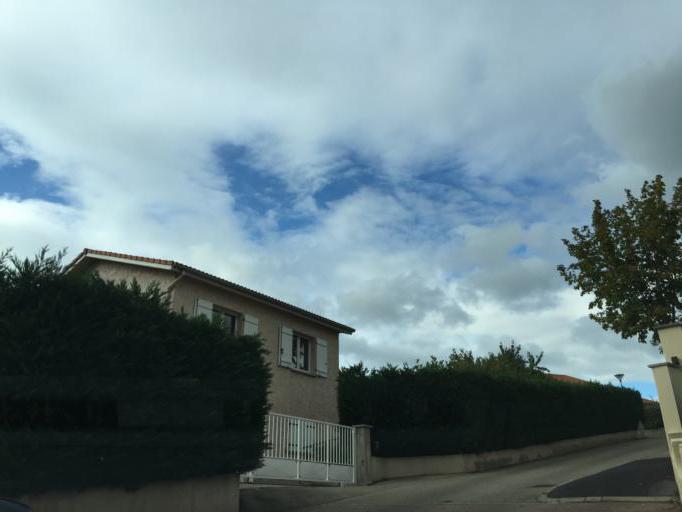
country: FR
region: Rhone-Alpes
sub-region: Departement de la Loire
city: Saint-Chamond
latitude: 45.4830
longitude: 4.5220
